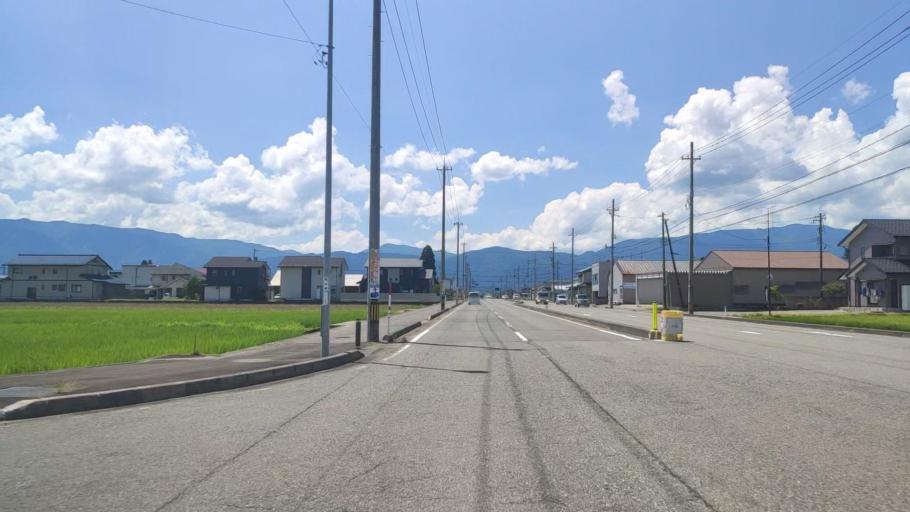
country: JP
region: Fukui
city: Ono
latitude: 35.9906
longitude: 136.5100
